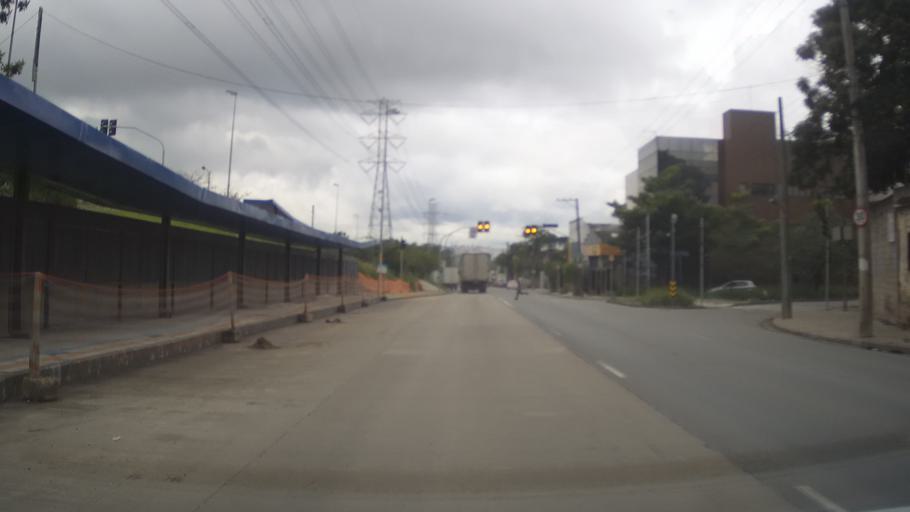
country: BR
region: Sao Paulo
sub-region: Guarulhos
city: Guarulhos
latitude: -23.4641
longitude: -46.4685
